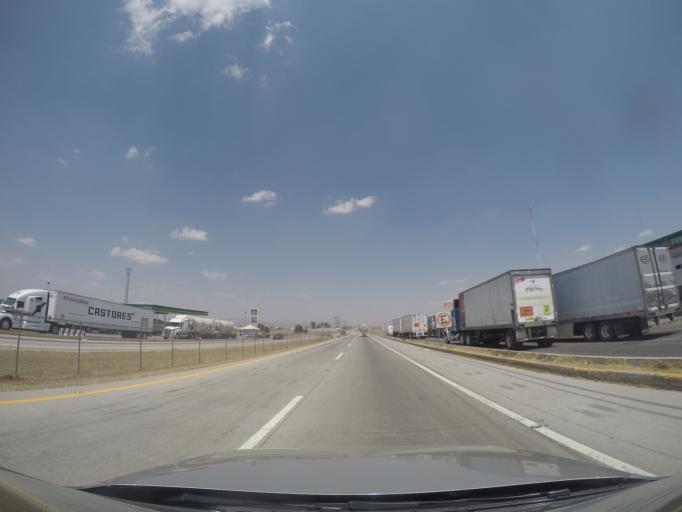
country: MX
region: Tlaxcala
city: Sanctorum
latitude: 19.5508
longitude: -98.4937
